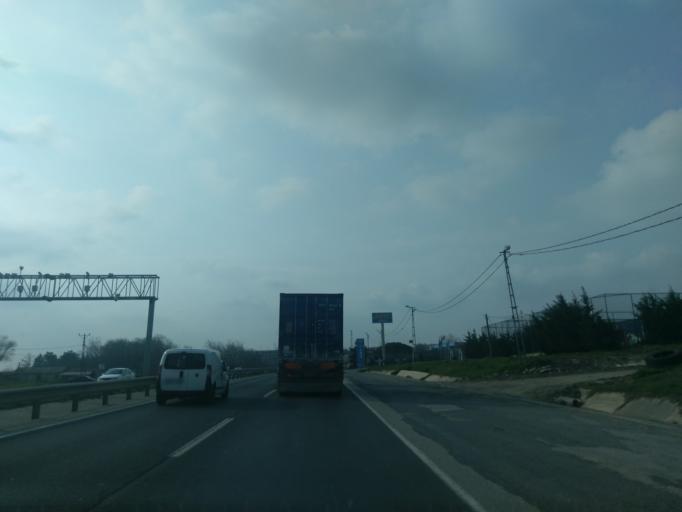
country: TR
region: Istanbul
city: Kavakli
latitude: 41.0689
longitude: 28.2948
